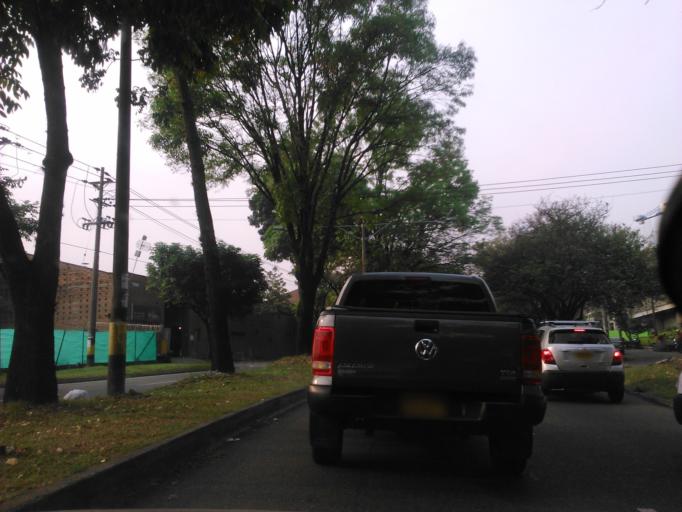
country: CO
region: Antioquia
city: Itagui
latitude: 6.2020
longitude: -75.5842
